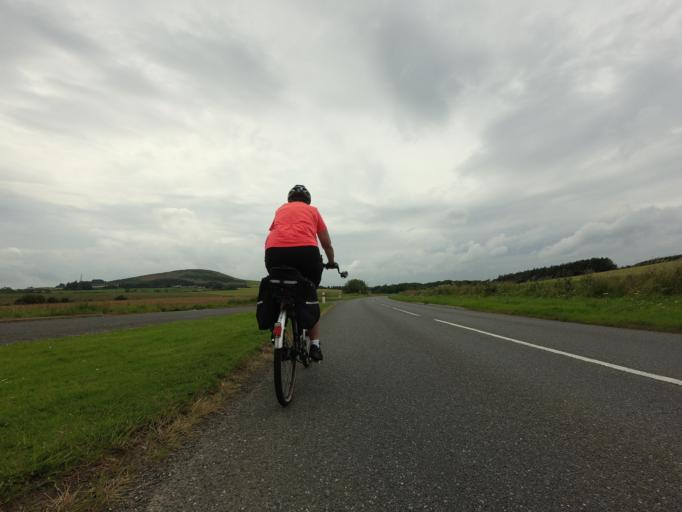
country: GB
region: Scotland
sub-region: Aberdeenshire
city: Portsoy
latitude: 57.6756
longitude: -2.7064
